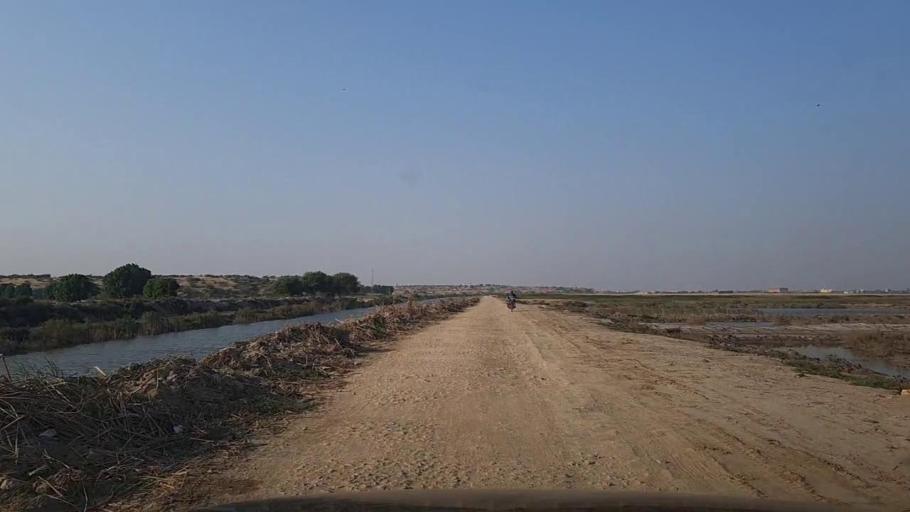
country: PK
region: Sindh
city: Thatta
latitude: 24.7310
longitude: 67.9075
